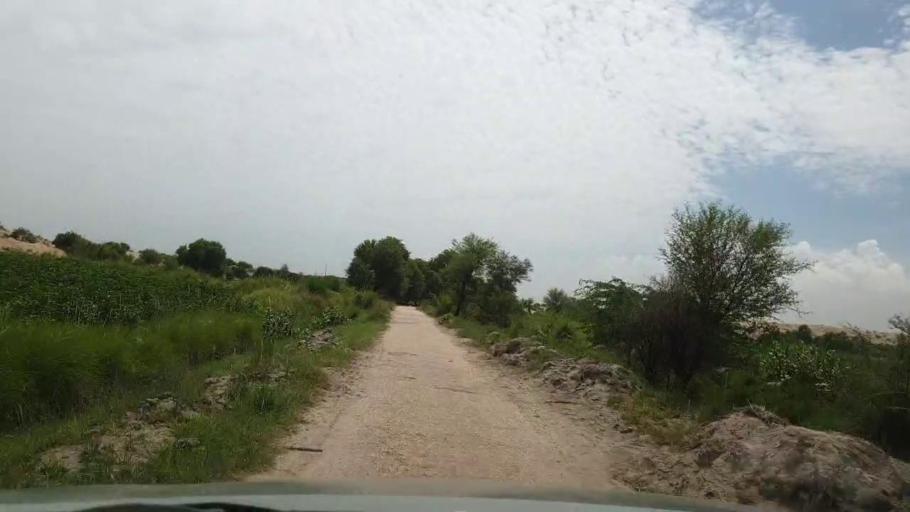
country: PK
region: Sindh
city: Bozdar
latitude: 27.0657
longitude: 68.9660
